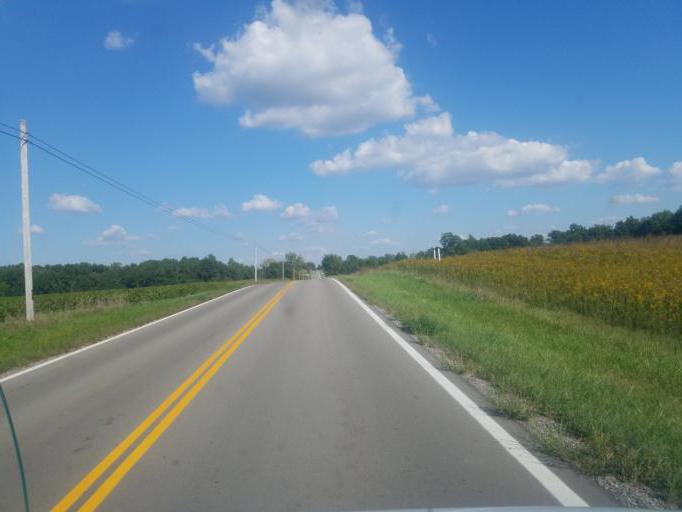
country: US
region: Ohio
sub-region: Shelby County
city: Jackson Center
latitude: 40.4685
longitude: -84.0866
